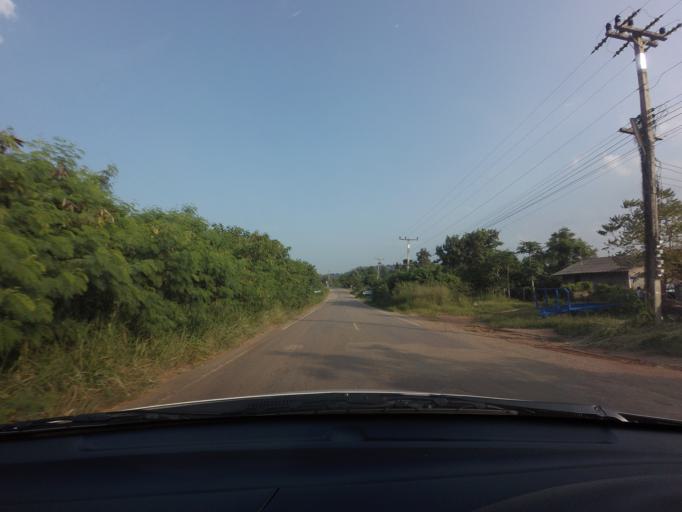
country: TH
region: Nakhon Ratchasima
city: Pak Chong
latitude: 14.5508
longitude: 101.5825
